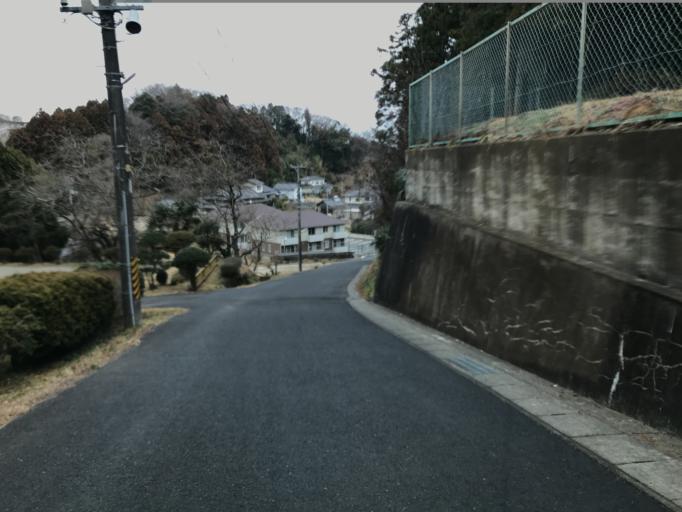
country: JP
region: Fukushima
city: Iwaki
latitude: 37.0608
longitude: 140.9067
